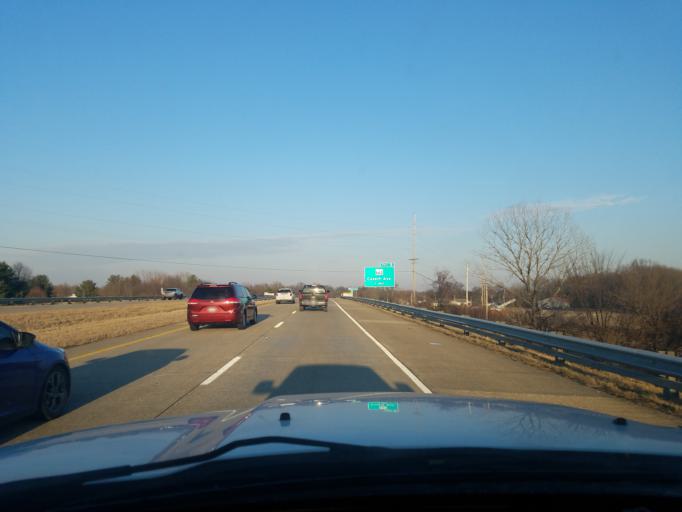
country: US
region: Indiana
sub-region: Warrick County
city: Newburgh
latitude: 37.9468
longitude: -87.4725
